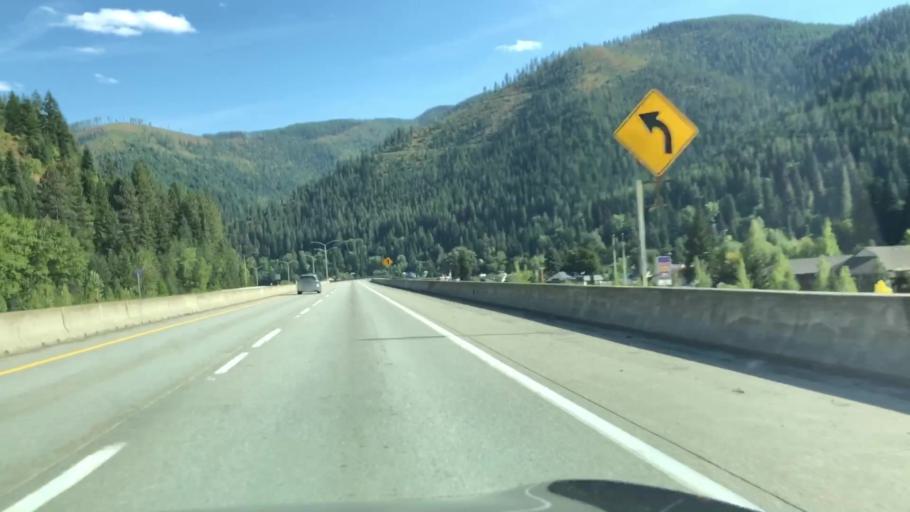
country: US
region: Idaho
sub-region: Shoshone County
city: Wallace
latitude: 47.4775
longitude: -115.9317
